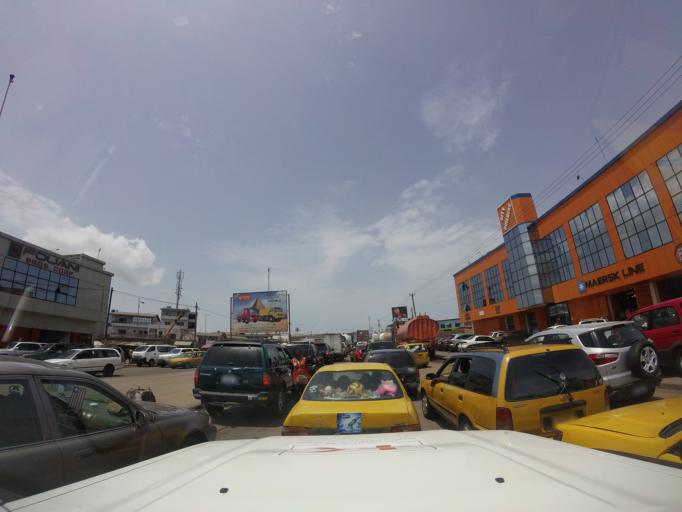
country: LR
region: Montserrado
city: Monrovia
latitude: 6.3361
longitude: -10.7946
